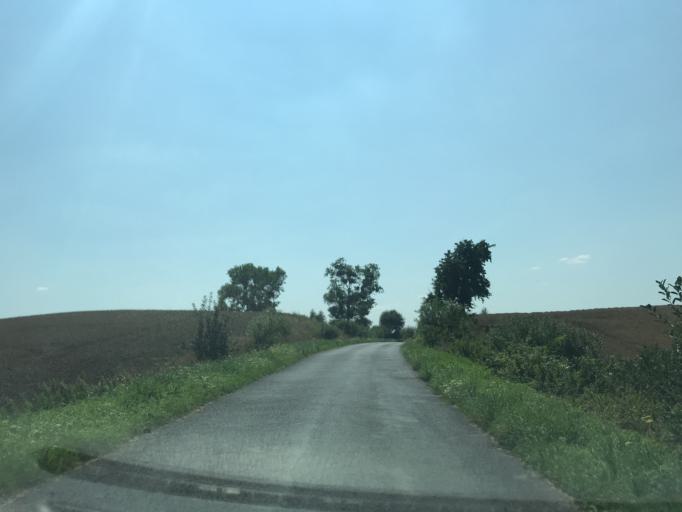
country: PL
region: Kujawsko-Pomorskie
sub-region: Powiat lipnowski
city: Chrostkowo
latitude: 52.9860
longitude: 19.2134
